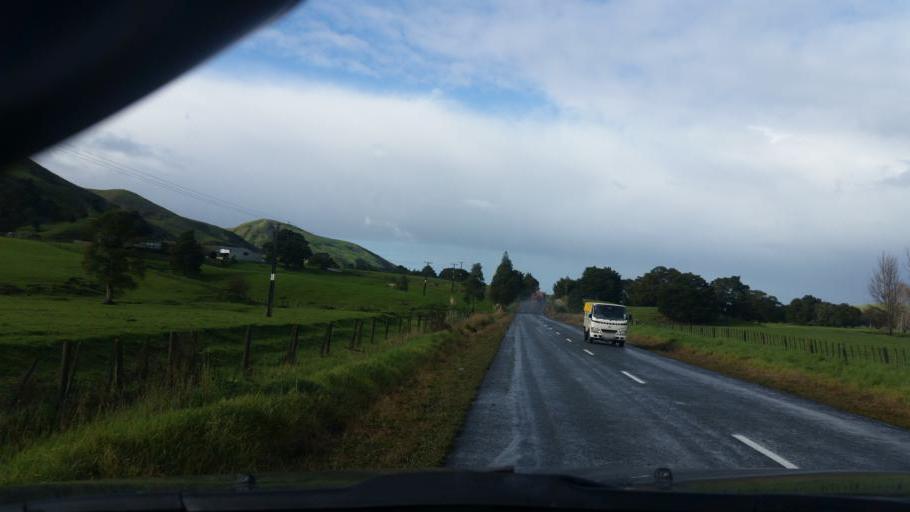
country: NZ
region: Northland
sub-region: Kaipara District
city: Dargaville
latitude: -35.8066
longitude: 173.9217
